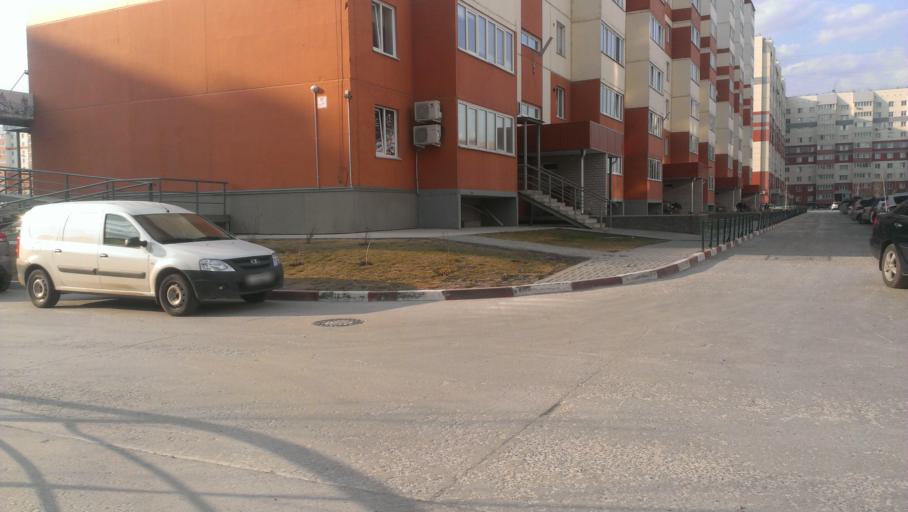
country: RU
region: Altai Krai
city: Novosilikatnyy
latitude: 53.3261
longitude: 83.6755
